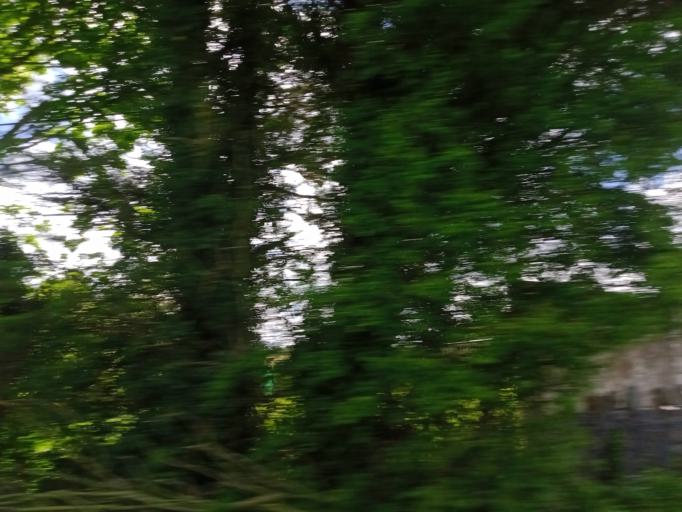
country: IE
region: Munster
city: Thurles
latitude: 52.6914
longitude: -7.6445
